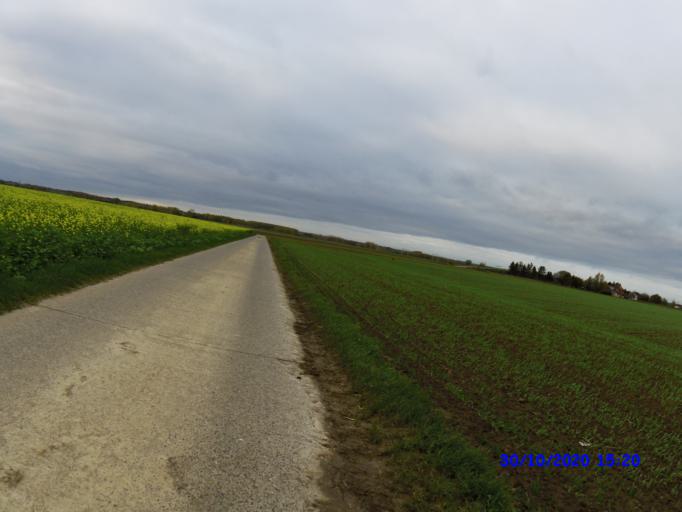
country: BE
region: Wallonia
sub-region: Province de Liege
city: Lincent
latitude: 50.7602
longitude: 5.0213
